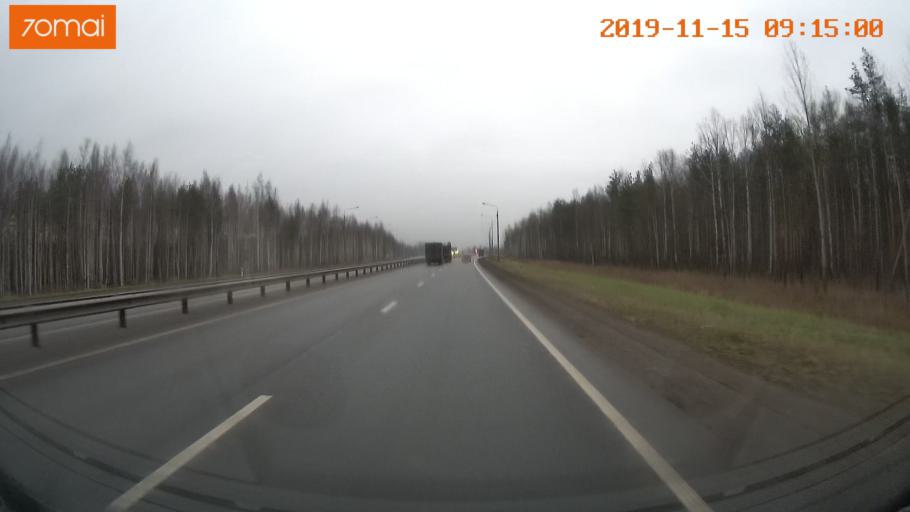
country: RU
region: Vologda
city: Tonshalovo
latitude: 59.2335
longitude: 37.9636
